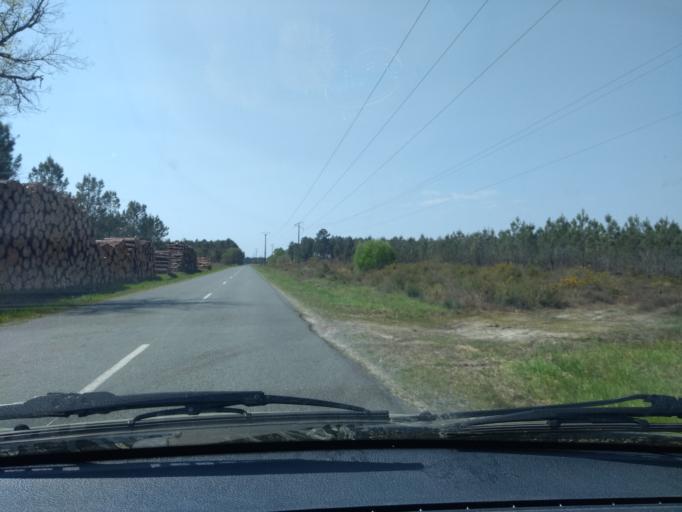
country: FR
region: Aquitaine
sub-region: Departement de la Gironde
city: Belin-Beliet
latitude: 44.5275
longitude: -0.7178
